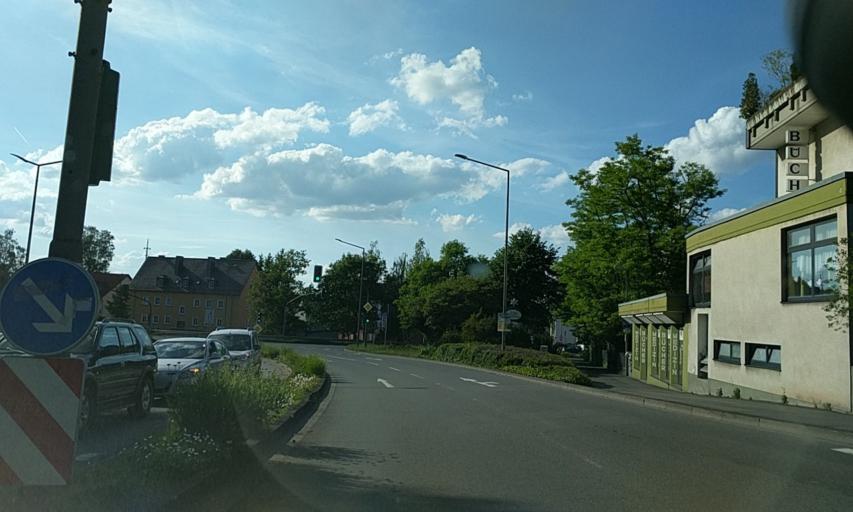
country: DE
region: Saarland
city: Homburg
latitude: 49.3119
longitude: 7.3445
